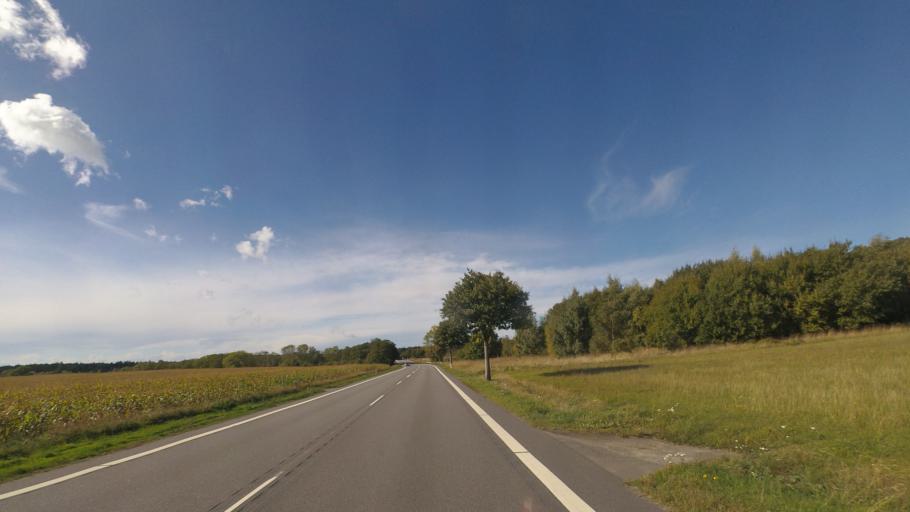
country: DK
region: Capital Region
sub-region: Bornholm Kommune
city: Ronne
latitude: 55.0774
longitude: 14.7698
